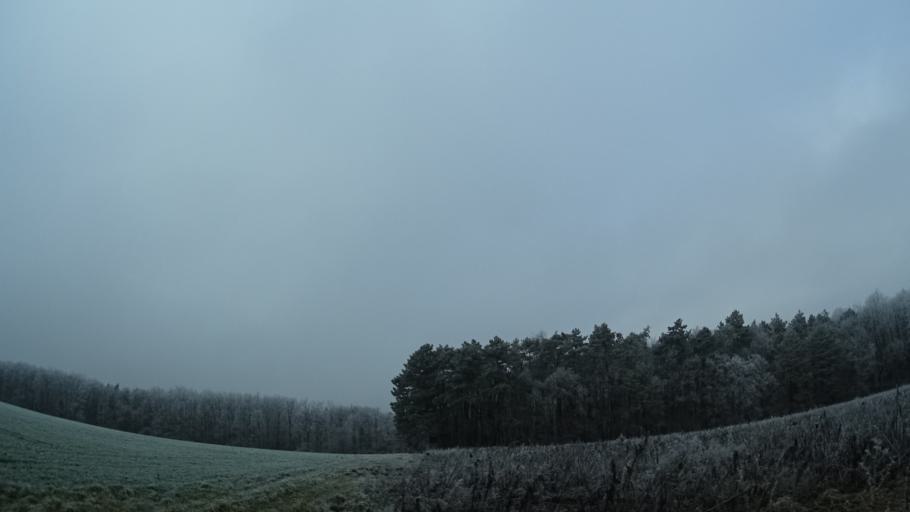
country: DE
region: Baden-Wuerttemberg
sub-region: Regierungsbezirk Stuttgart
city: Boxberg
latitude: 49.5195
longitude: 9.6460
